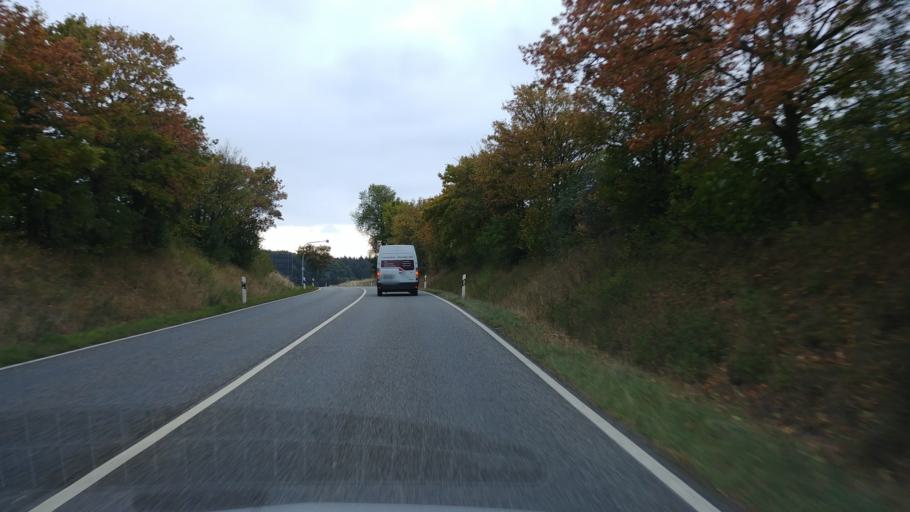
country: DE
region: Hesse
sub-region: Regierungsbezirk Darmstadt
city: Idstein
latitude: 50.2444
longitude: 8.1884
